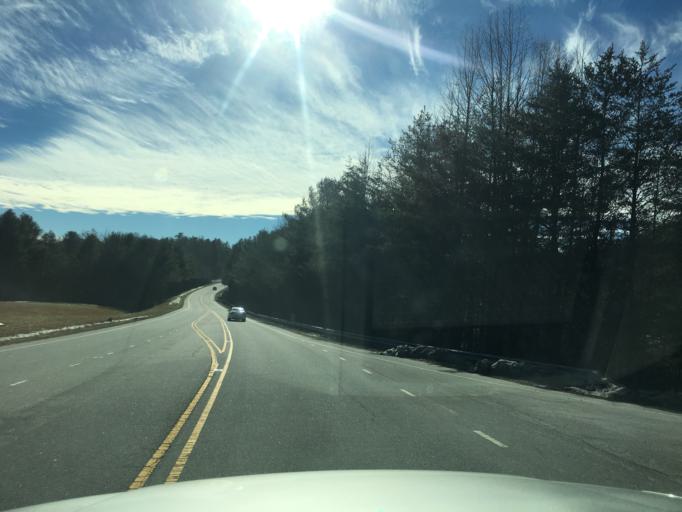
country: US
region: North Carolina
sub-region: Transylvania County
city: Brevard
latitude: 35.1801
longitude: -82.8002
